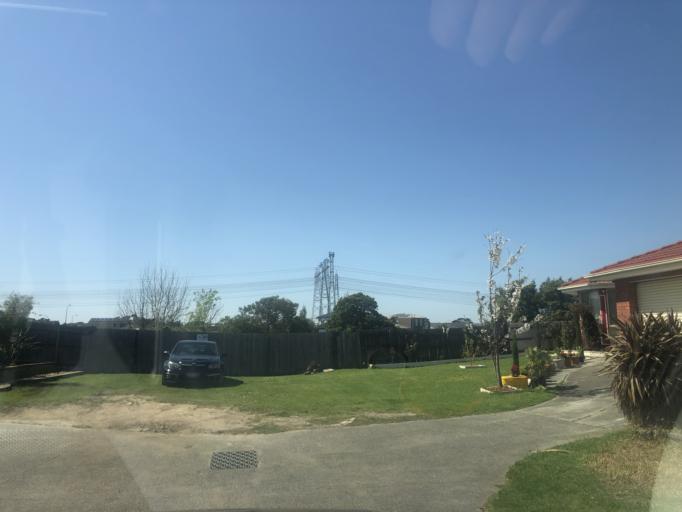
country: AU
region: Victoria
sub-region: Casey
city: Narre Warren South
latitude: -38.0499
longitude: 145.2787
